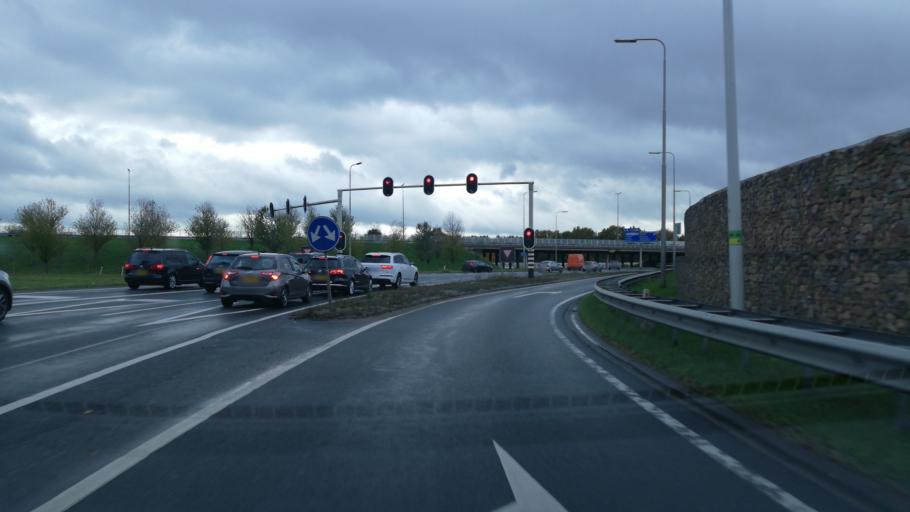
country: NL
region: Overijssel
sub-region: Gemeente Zwolle
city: Zwolle
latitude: 52.5075
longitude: 6.0653
